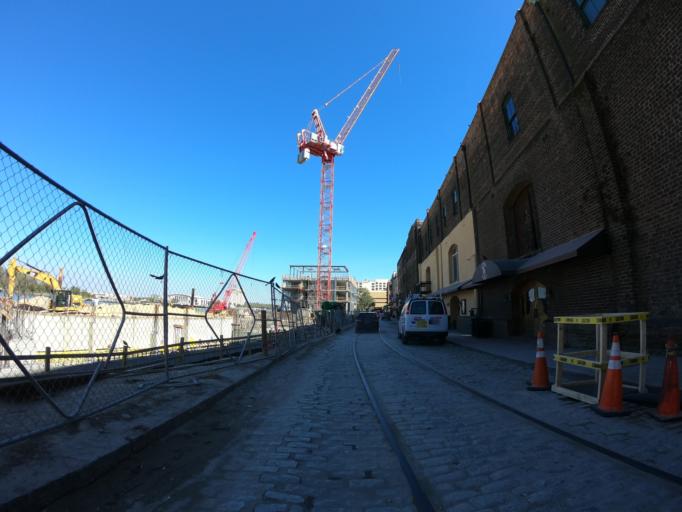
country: US
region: Georgia
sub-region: Chatham County
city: Savannah
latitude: 32.0830
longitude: -81.0950
